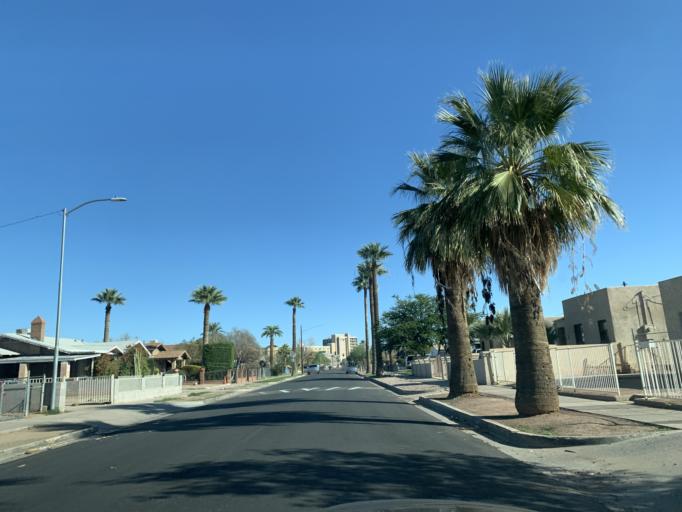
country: US
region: Arizona
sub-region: Maricopa County
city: Phoenix
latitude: 33.4548
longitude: -112.0501
